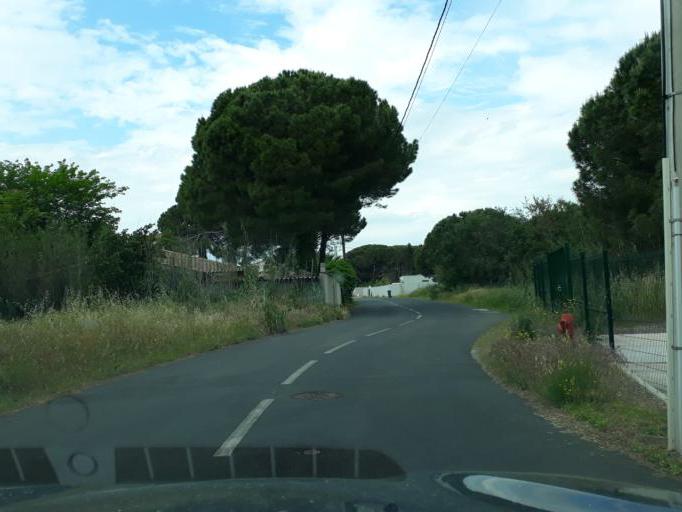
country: FR
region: Languedoc-Roussillon
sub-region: Departement de l'Herault
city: Agde
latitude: 43.2869
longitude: 3.4675
